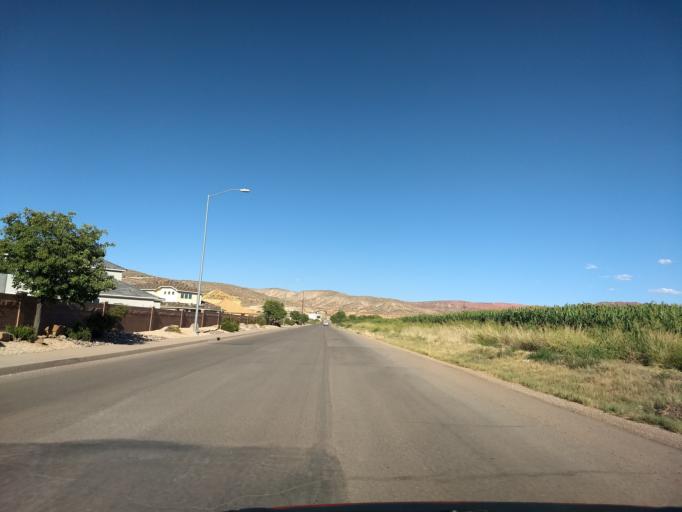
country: US
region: Utah
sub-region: Washington County
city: Washington
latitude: 37.0960
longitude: -113.5128
